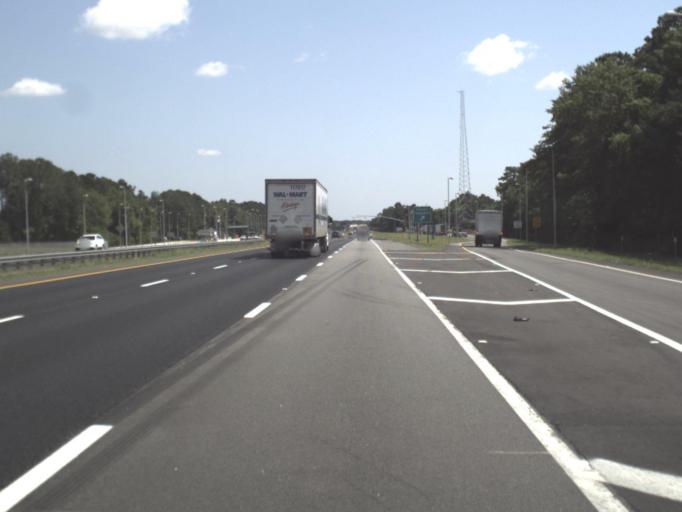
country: US
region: Georgia
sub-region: Camden County
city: Kingsland
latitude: 30.7228
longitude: -81.6653
